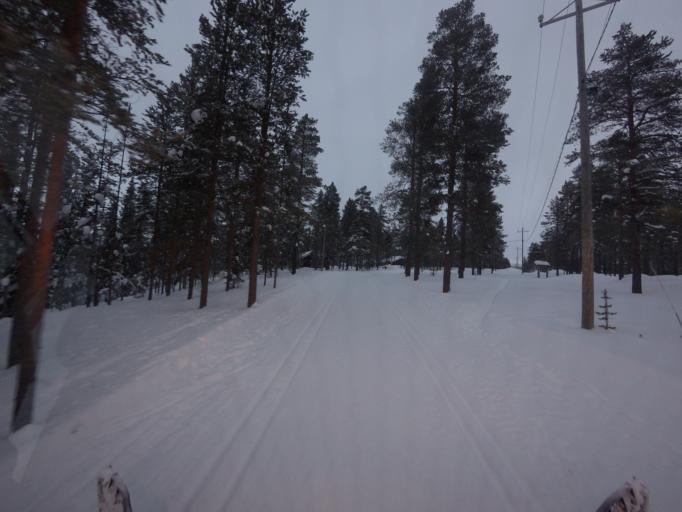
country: FI
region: Lapland
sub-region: Tunturi-Lappi
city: Kolari
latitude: 67.6196
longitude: 24.1691
